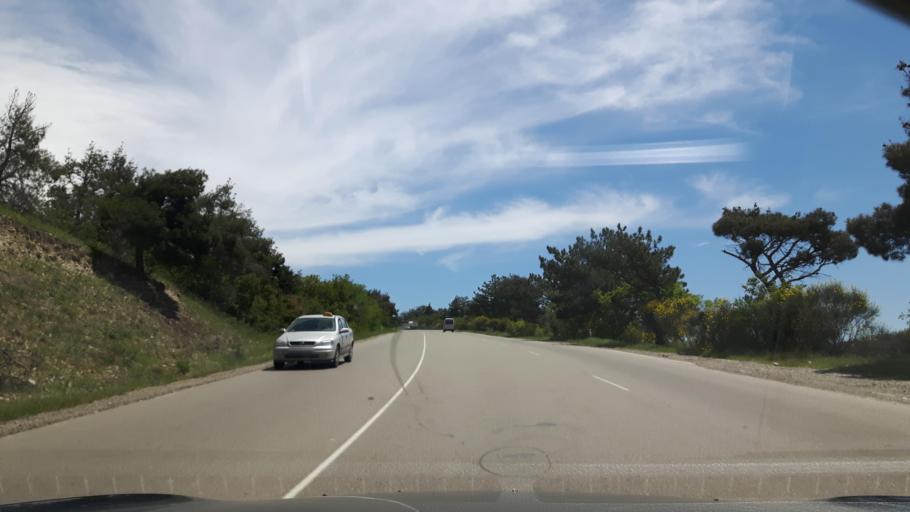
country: GE
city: Didi Lilo
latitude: 41.6939
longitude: 45.0863
